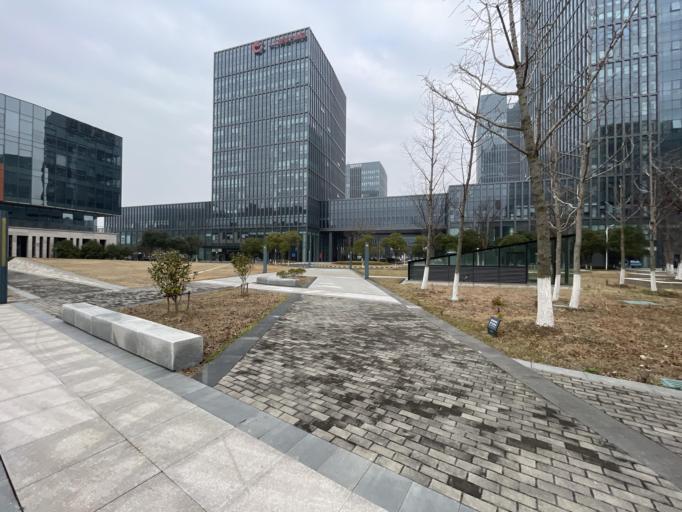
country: CN
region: Jiangsu Sheng
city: Shengpu
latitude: 31.2949
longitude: 120.7694
